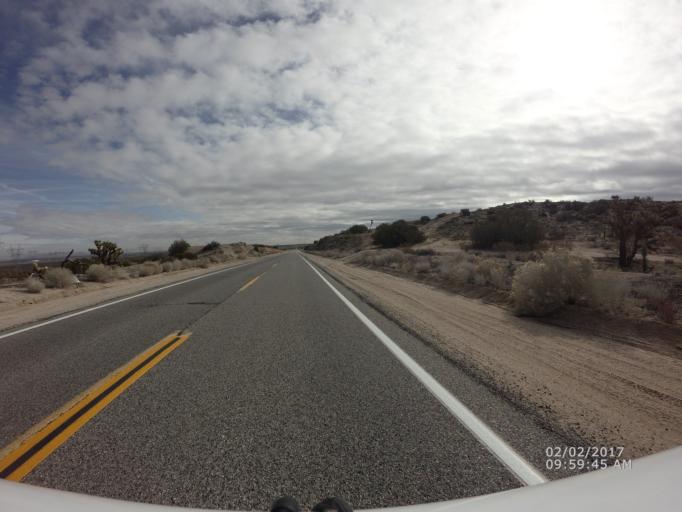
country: US
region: California
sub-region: Los Angeles County
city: Littlerock
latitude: 34.5066
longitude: -117.9792
